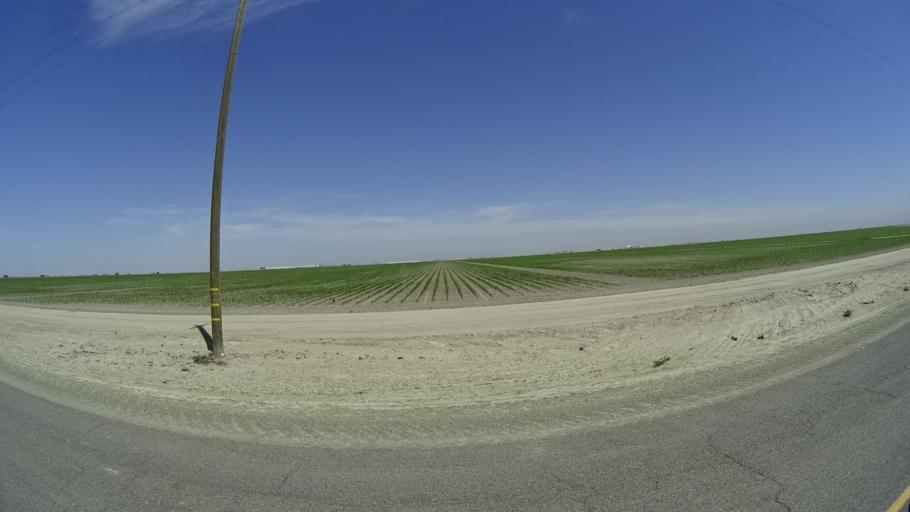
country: US
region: California
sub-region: Kings County
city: Corcoran
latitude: 36.1379
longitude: -119.6832
